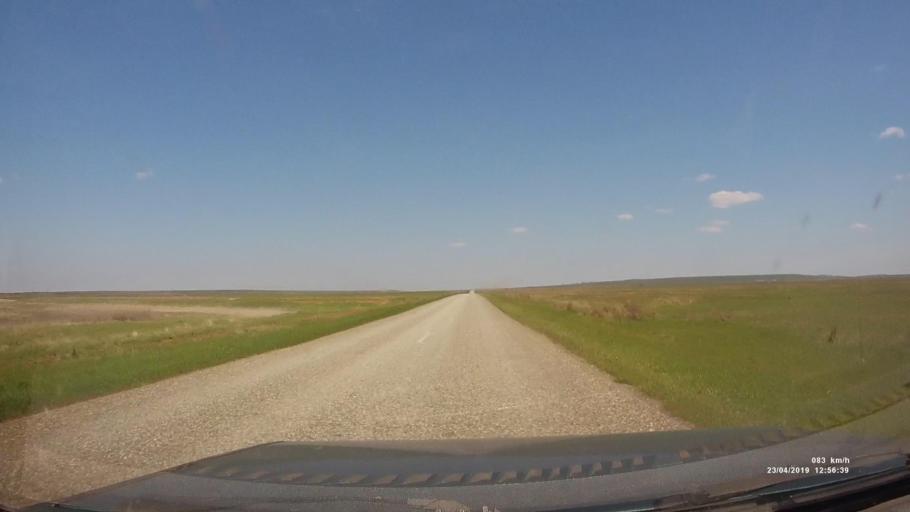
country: RU
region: Kalmykiya
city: Yashalta
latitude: 46.5961
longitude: 42.5735
